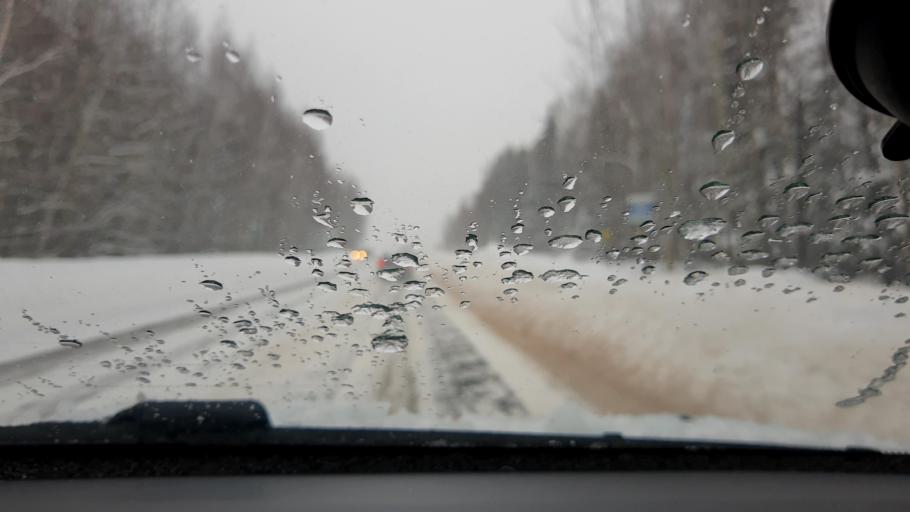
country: RU
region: Nizjnij Novgorod
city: Pervomayskiy
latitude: 56.6359
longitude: 43.2497
